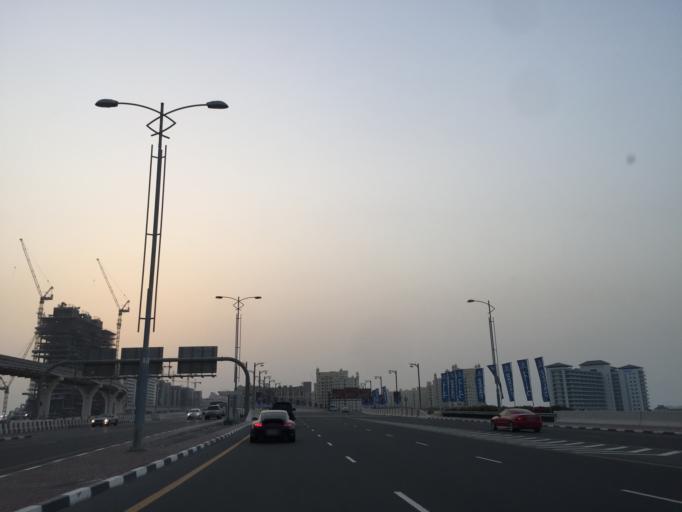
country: AE
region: Dubai
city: Dubai
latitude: 25.1019
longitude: 55.1549
